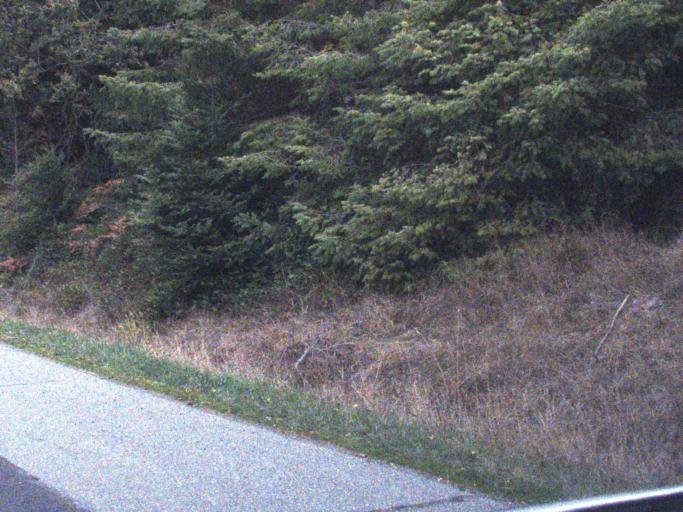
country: US
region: Washington
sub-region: Island County
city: Camano
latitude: 48.1597
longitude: -122.6035
